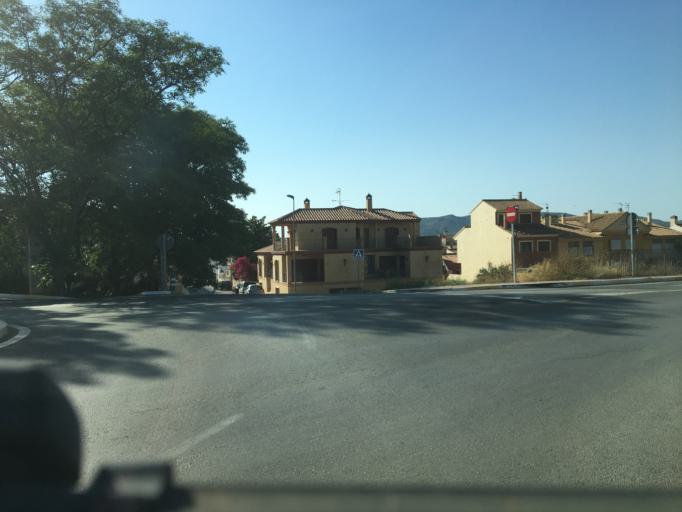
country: ES
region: Murcia
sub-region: Murcia
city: Puerto Lumbreras
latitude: 37.5579
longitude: -1.8097
